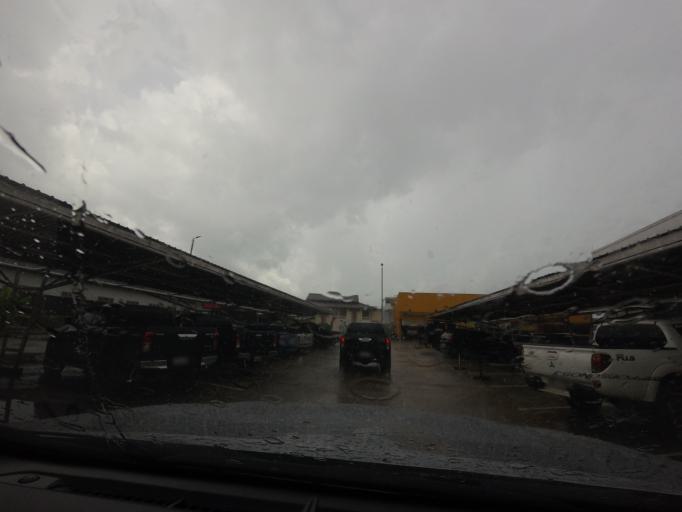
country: TH
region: Chumphon
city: Chumphon
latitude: 10.5033
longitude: 99.1393
